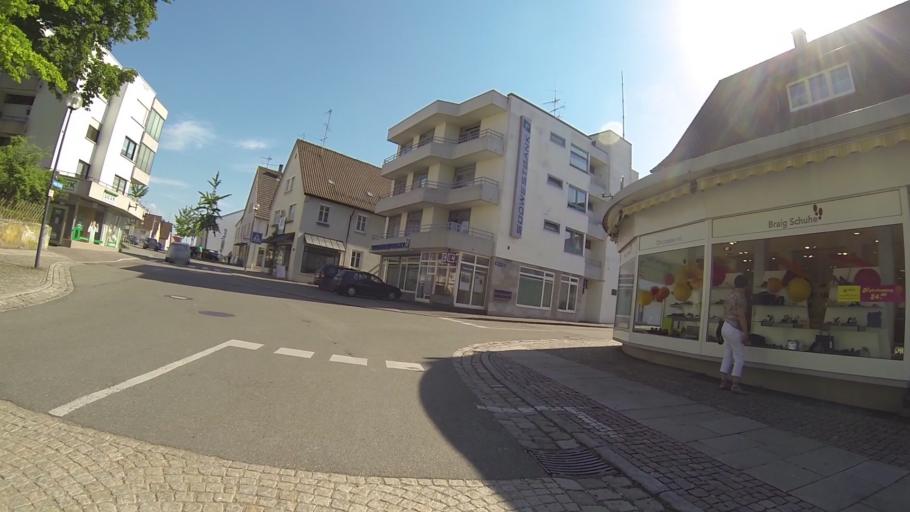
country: DE
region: Baden-Wuerttemberg
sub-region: Tuebingen Region
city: Laupheim
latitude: 48.2283
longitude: 9.8853
